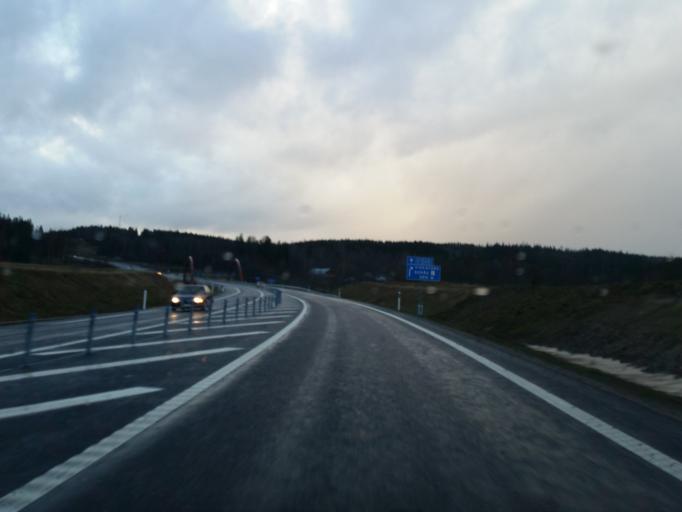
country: SE
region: Vaestra Goetaland
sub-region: Boras Kommun
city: Boras
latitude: 57.6957
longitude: 12.9170
